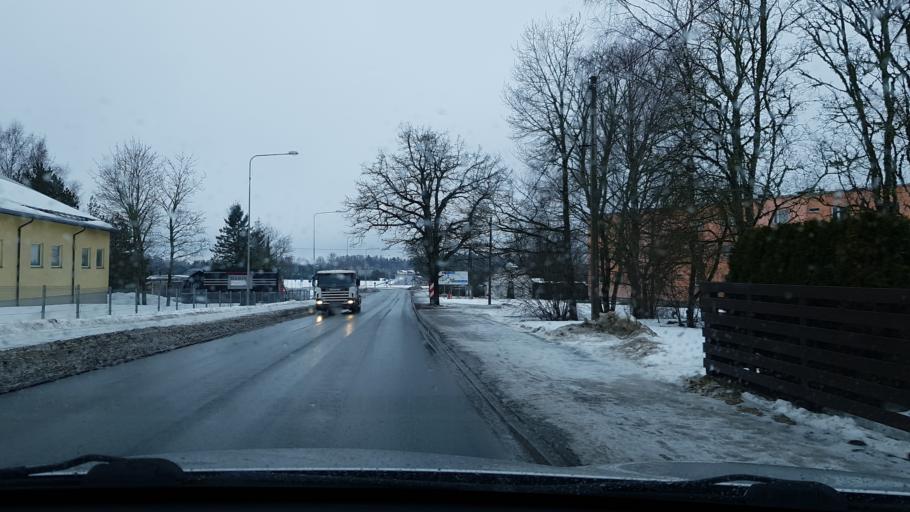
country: EE
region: Raplamaa
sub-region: Rapla vald
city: Rapla
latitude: 58.9972
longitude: 24.7906
